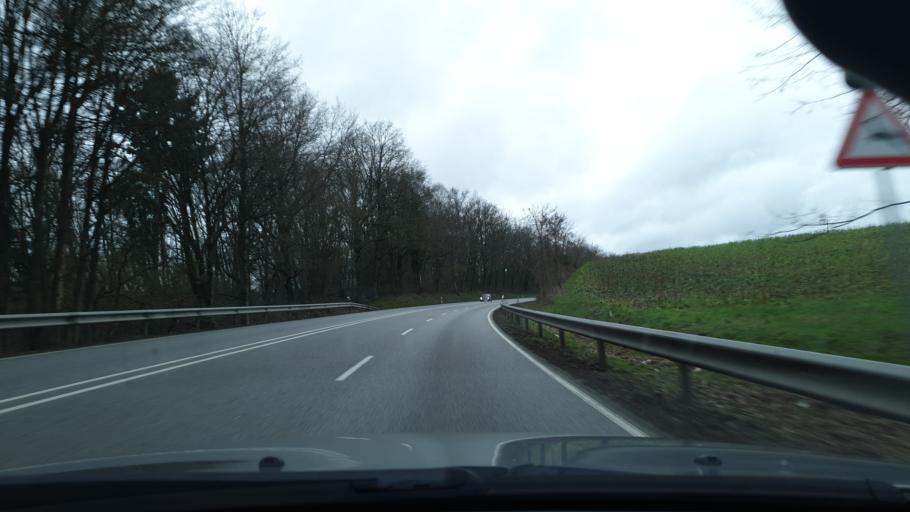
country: DE
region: Rheinland-Pfalz
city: Zweibrucken
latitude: 49.2620
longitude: 7.3744
